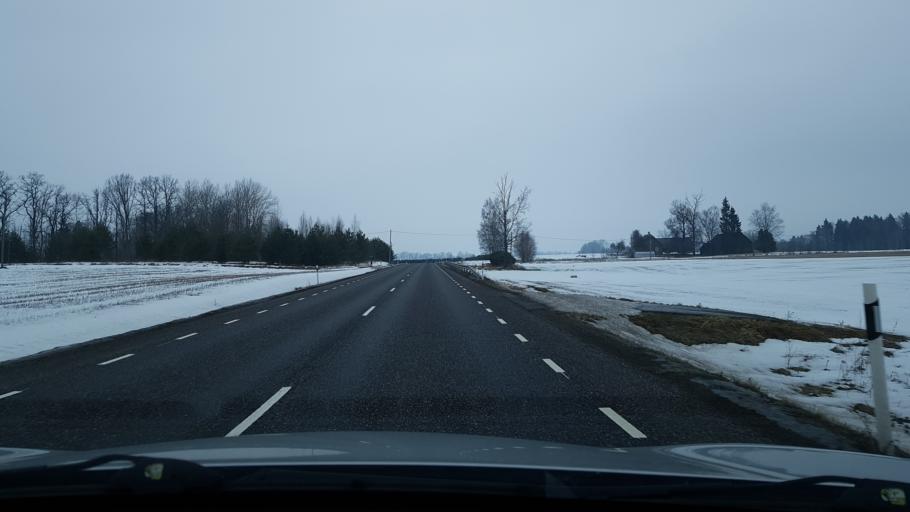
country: EE
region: Vorumaa
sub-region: Antsla vald
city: Vana-Antsla
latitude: 57.8943
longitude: 26.2891
